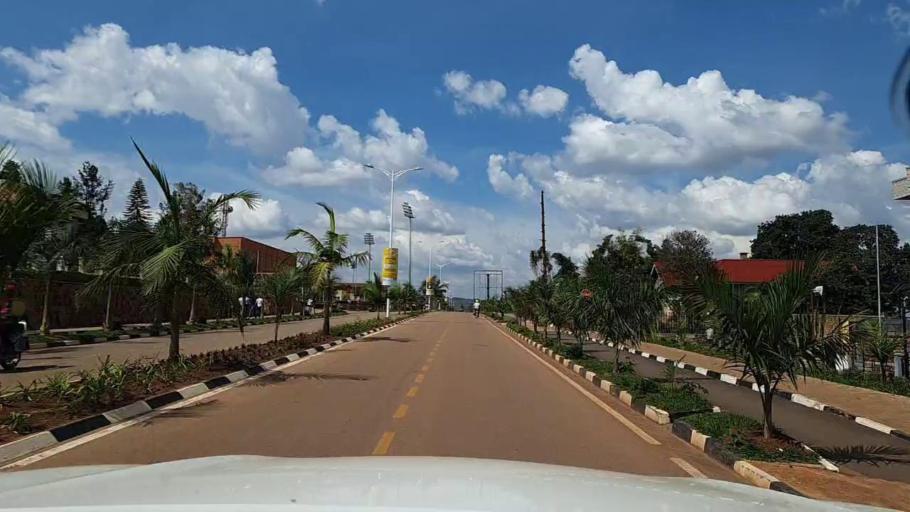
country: RW
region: Southern Province
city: Butare
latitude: -2.5997
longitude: 29.7421
